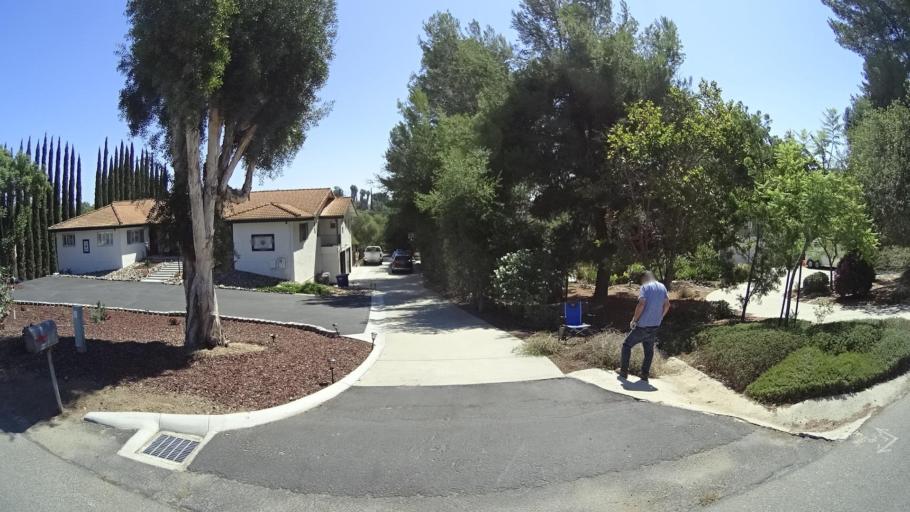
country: US
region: California
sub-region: San Diego County
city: Fallbrook
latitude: 33.3597
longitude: -117.2195
